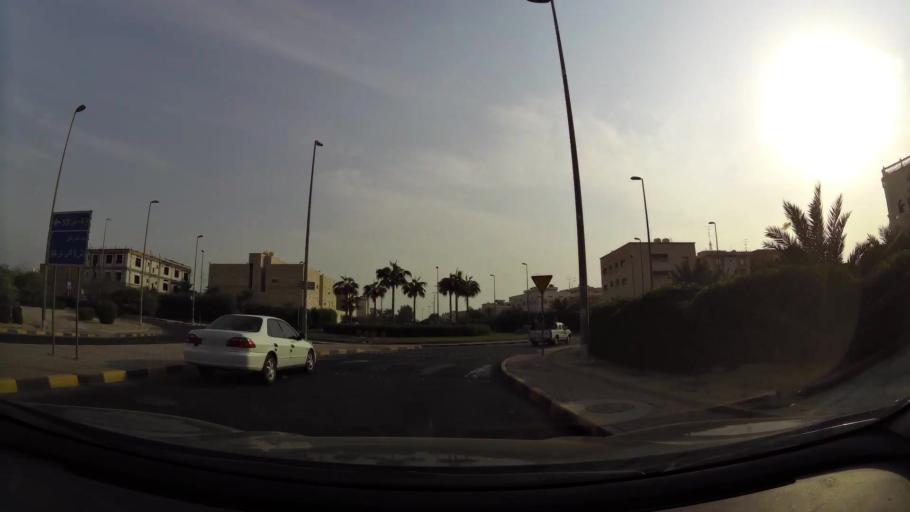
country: KW
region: Mubarak al Kabir
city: Mubarak al Kabir
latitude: 29.1989
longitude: 48.0686
